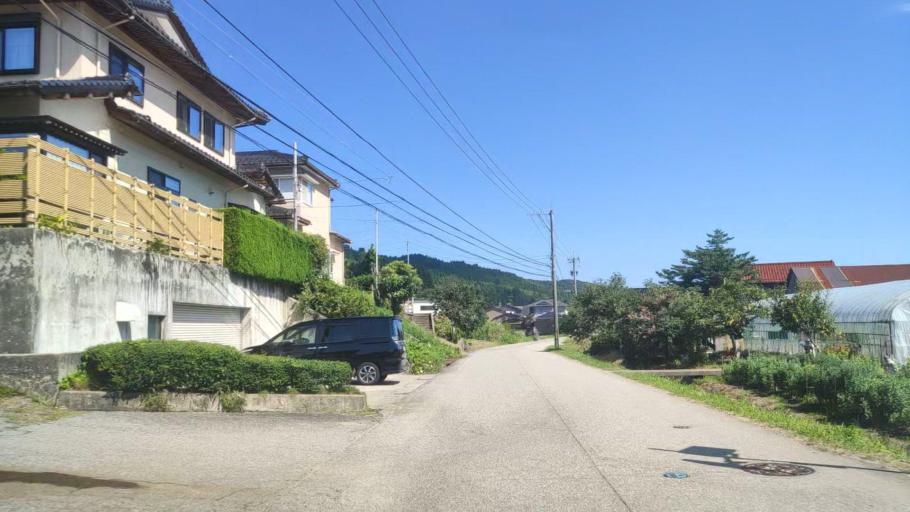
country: JP
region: Ishikawa
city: Nanao
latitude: 37.3733
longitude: 136.8745
